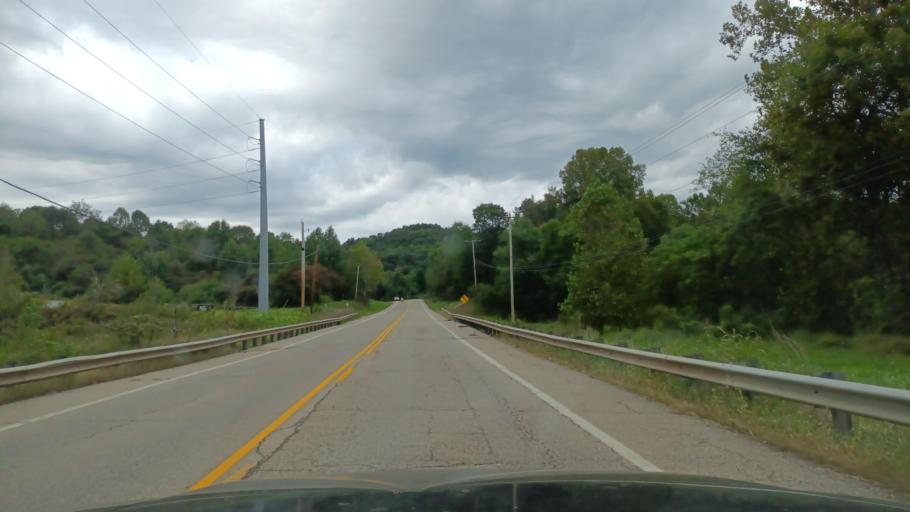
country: US
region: Ohio
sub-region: Vinton County
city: McArthur
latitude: 39.2412
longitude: -82.4530
